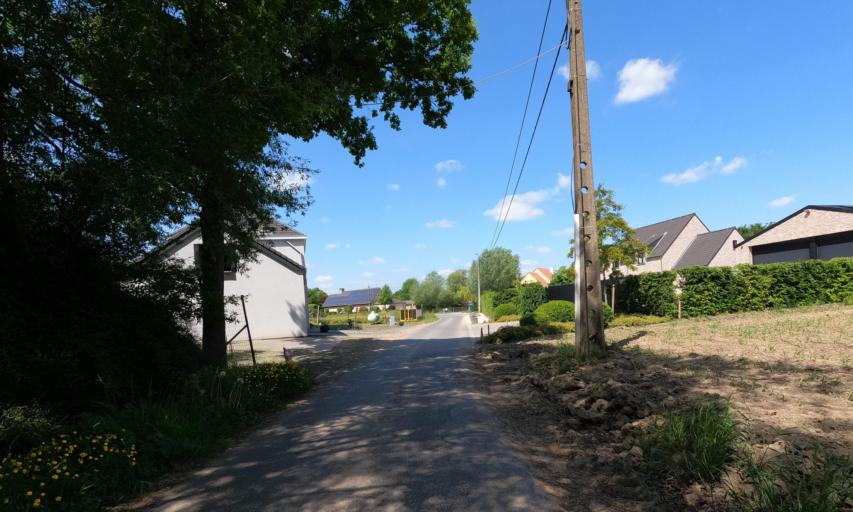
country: BE
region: Flanders
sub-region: Provincie Vlaams-Brabant
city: Merchtem
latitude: 50.9592
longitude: 4.2574
